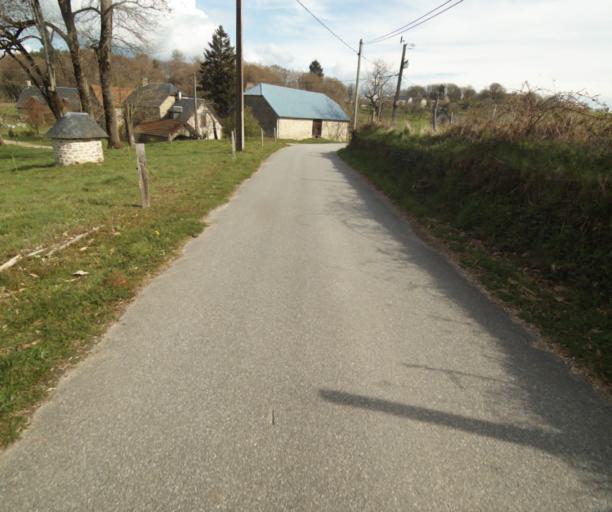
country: FR
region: Limousin
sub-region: Departement de la Correze
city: Correze
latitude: 45.3510
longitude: 1.8592
